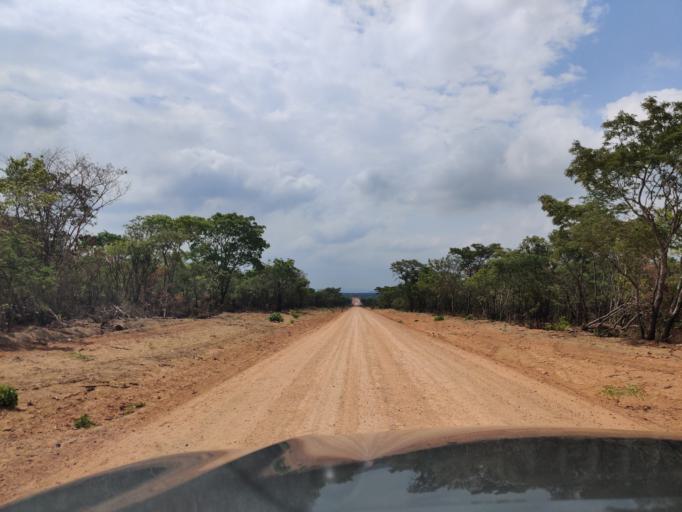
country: ZM
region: Central
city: Mkushi
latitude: -13.6738
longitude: 29.7522
